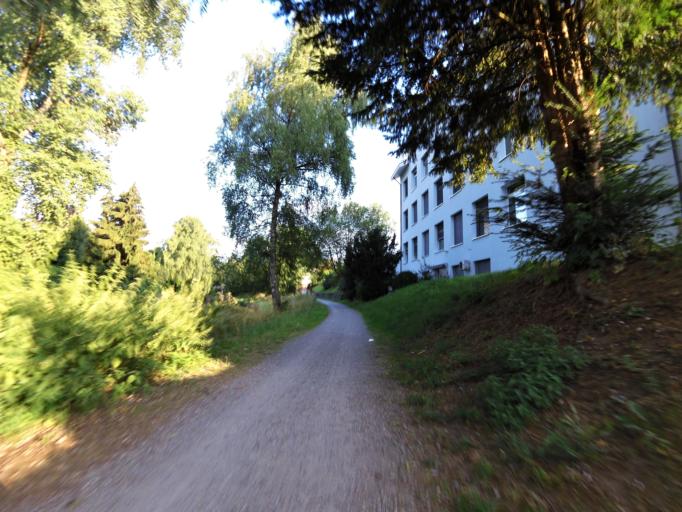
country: CH
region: Zurich
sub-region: Bezirk Buelach
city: Glattbrugg / Wydacker/Bettacker/Laettenwiesen
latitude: 47.4330
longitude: 8.5670
